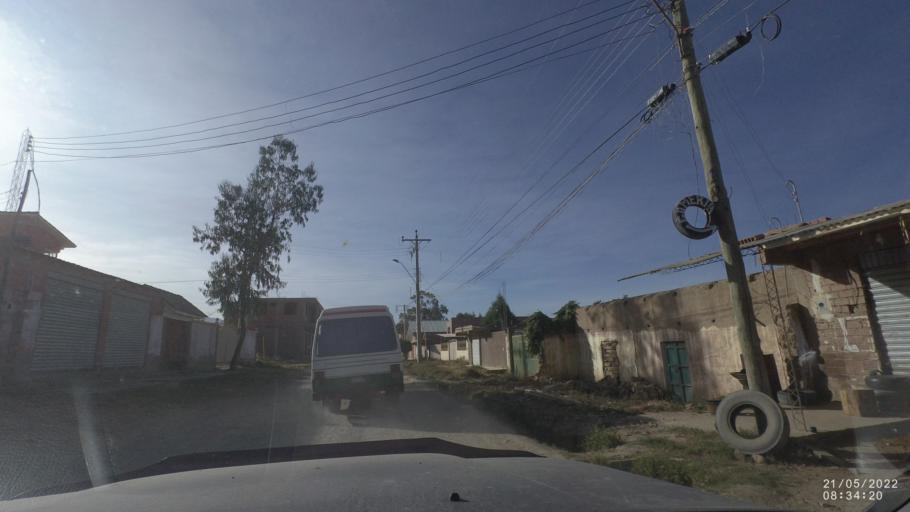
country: BO
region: Cochabamba
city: Cochabamba
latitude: -17.3871
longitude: -66.0465
